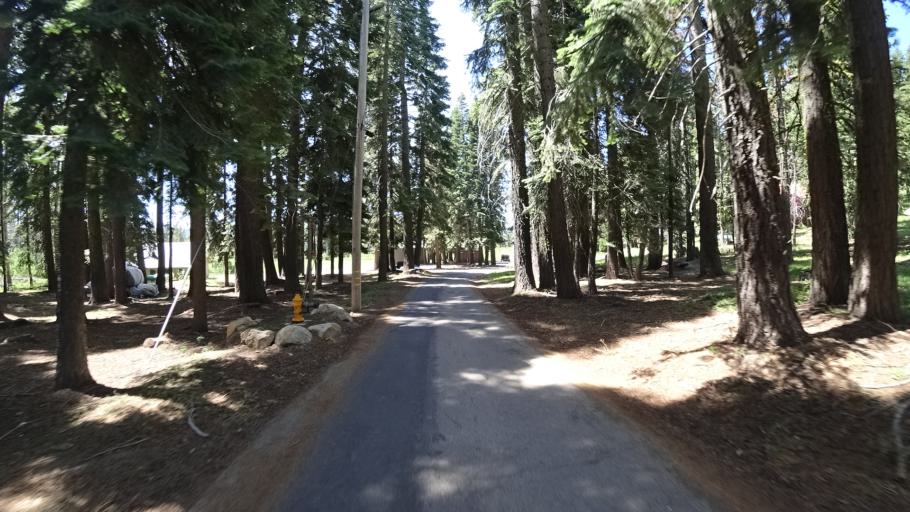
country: US
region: California
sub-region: Calaveras County
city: Arnold
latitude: 38.4280
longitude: -120.0932
